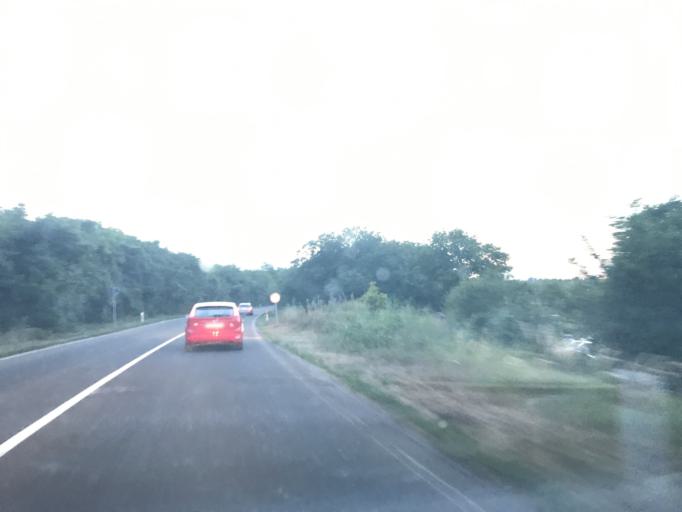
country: RS
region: Central Serbia
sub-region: Branicevski Okrug
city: Pozarevac
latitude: 44.6471
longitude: 21.2099
